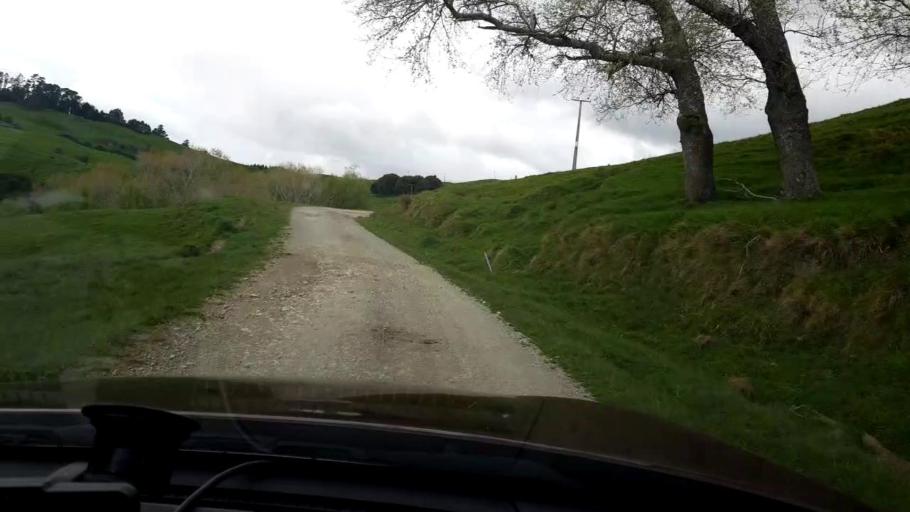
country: NZ
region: Gisborne
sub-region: Gisborne District
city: Gisborne
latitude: -38.3666
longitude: 177.9567
